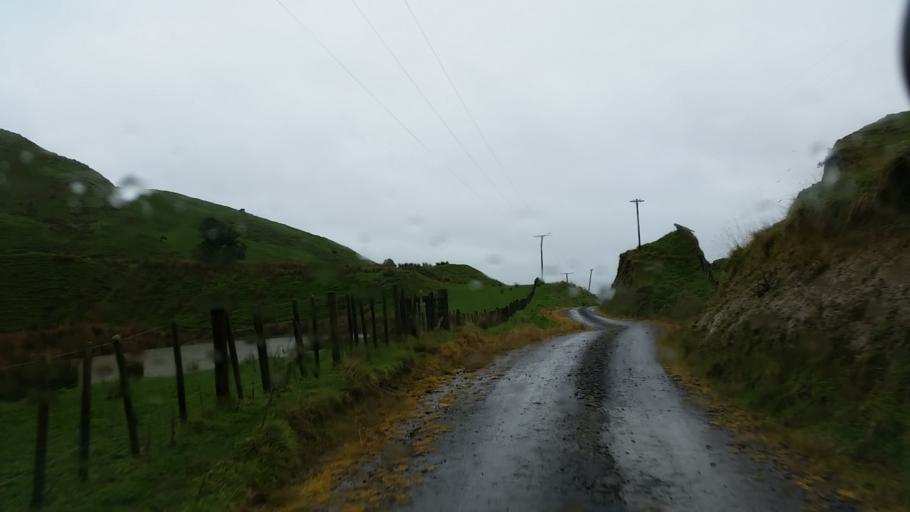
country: NZ
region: Taranaki
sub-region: South Taranaki District
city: Eltham
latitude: -39.4759
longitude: 174.4126
